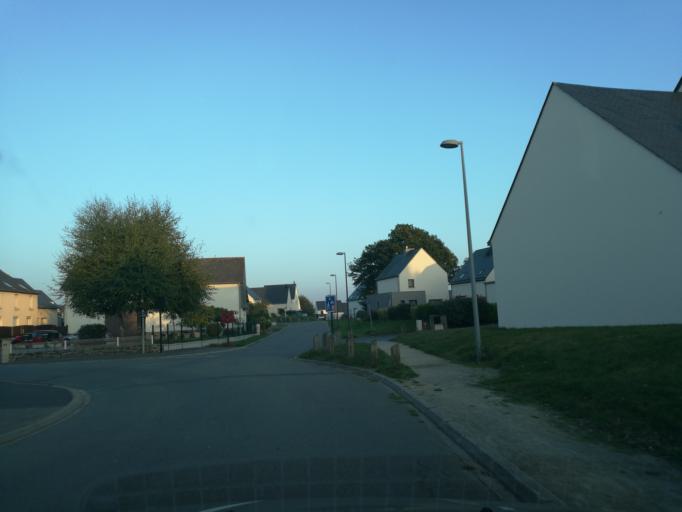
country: FR
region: Brittany
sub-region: Departement d'Ille-et-Vilaine
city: Pleumeleuc
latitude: 48.1828
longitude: -1.9175
